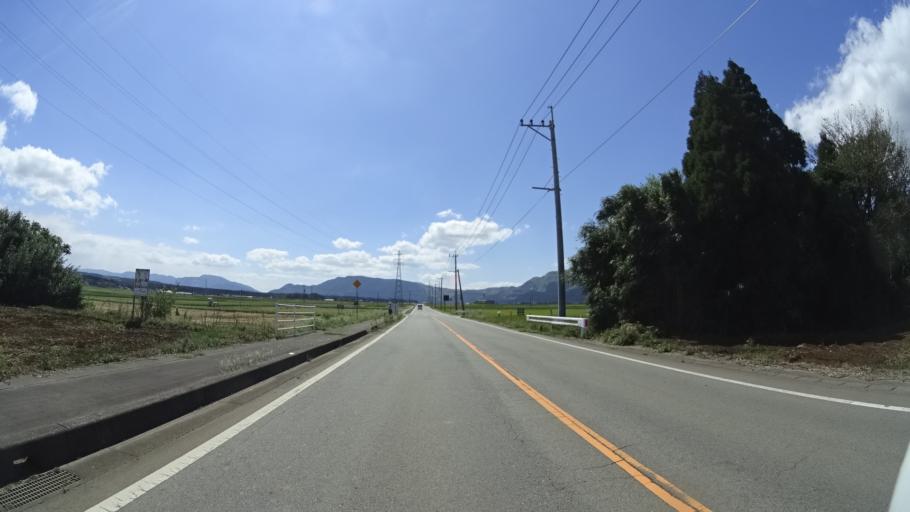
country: JP
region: Kumamoto
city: Aso
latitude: 32.9411
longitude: 131.0225
